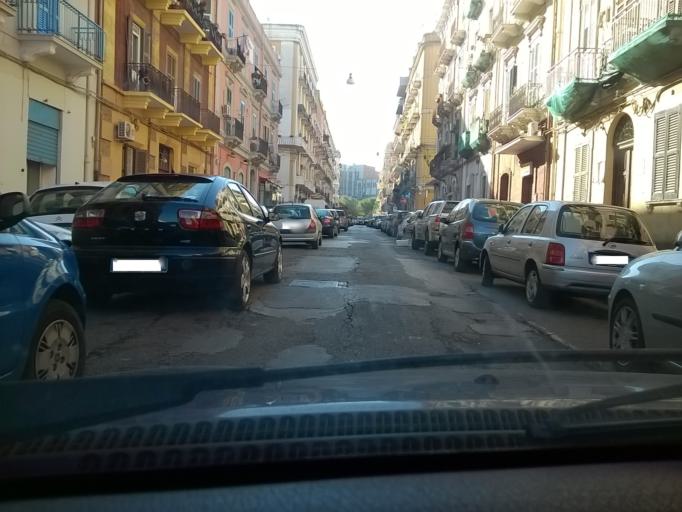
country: IT
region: Apulia
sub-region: Provincia di Taranto
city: Taranto
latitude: 40.4681
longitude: 17.2500
